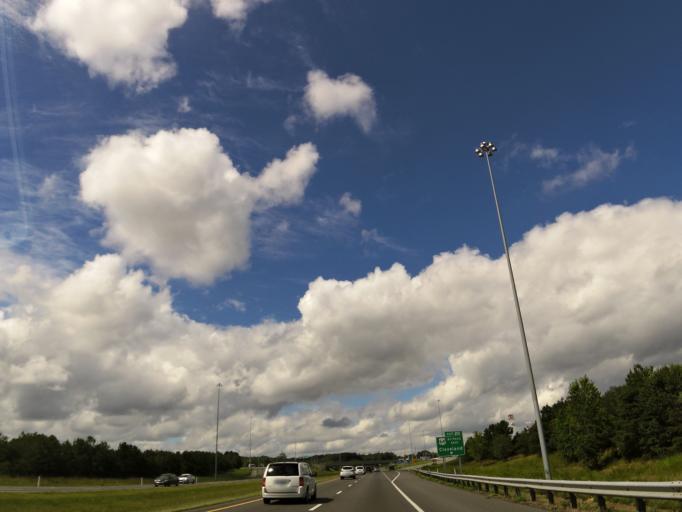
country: US
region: Tennessee
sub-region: Bradley County
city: Cleveland
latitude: 35.1554
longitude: -84.9428
